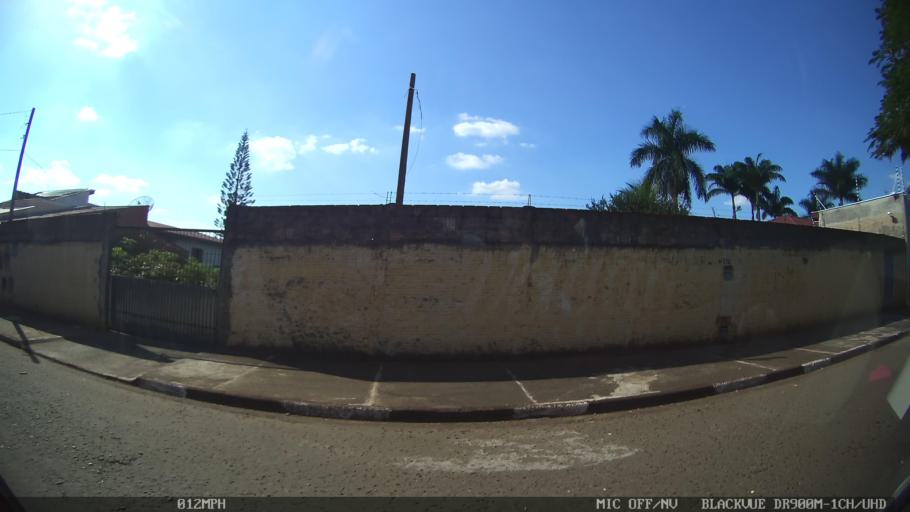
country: BR
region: Sao Paulo
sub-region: Sumare
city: Sumare
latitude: -22.8122
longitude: -47.2884
